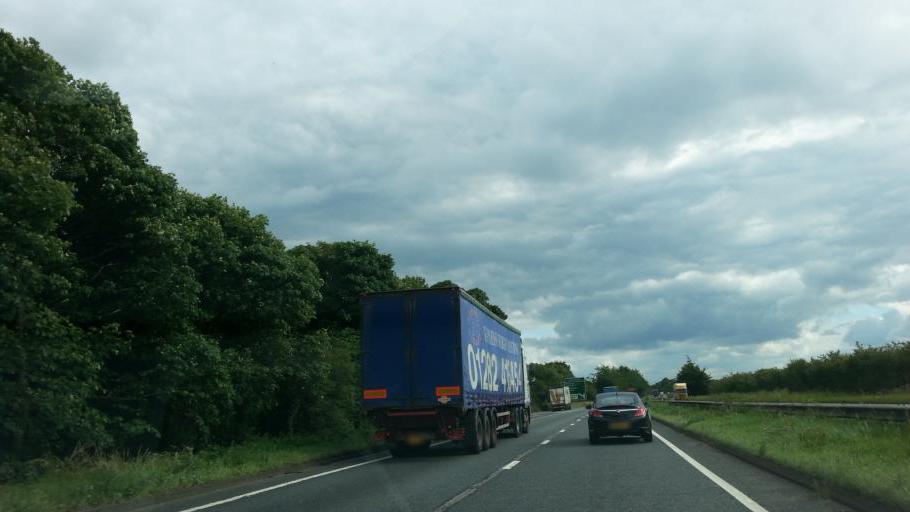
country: GB
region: England
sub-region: Nottinghamshire
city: Babworth
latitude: 53.3086
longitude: -1.0299
